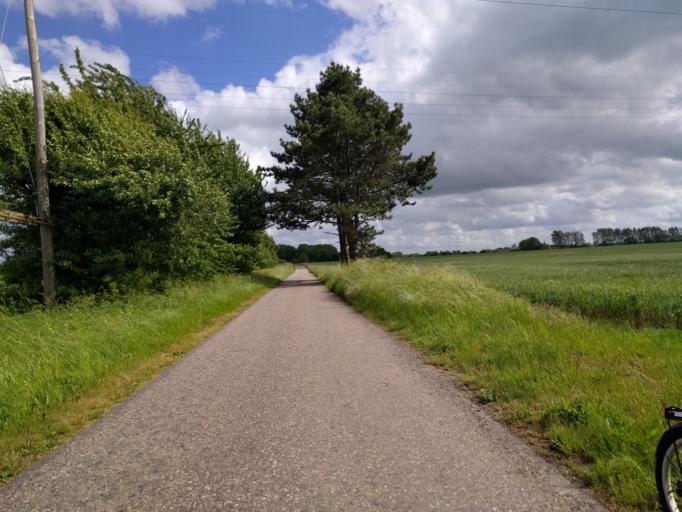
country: DK
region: South Denmark
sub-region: Kerteminde Kommune
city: Munkebo
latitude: 55.4541
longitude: 10.5161
